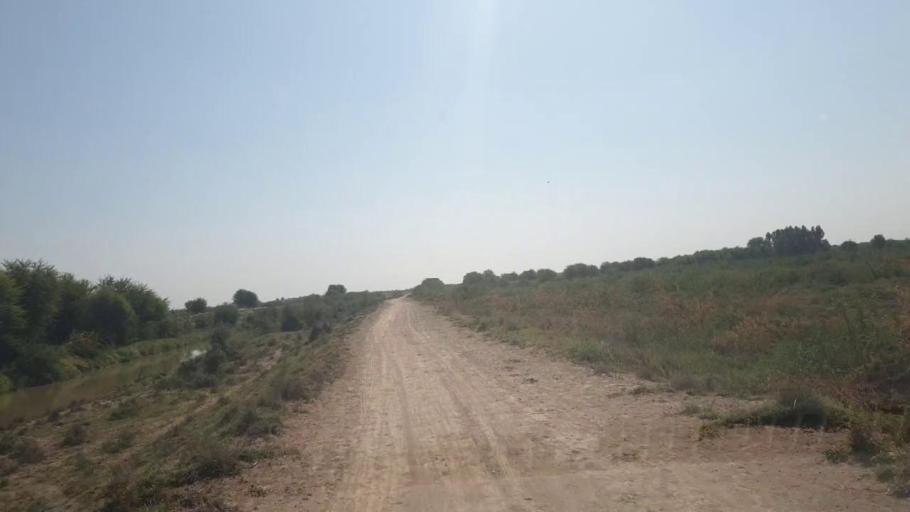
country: PK
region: Sindh
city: Digri
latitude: 24.9316
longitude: 69.1640
